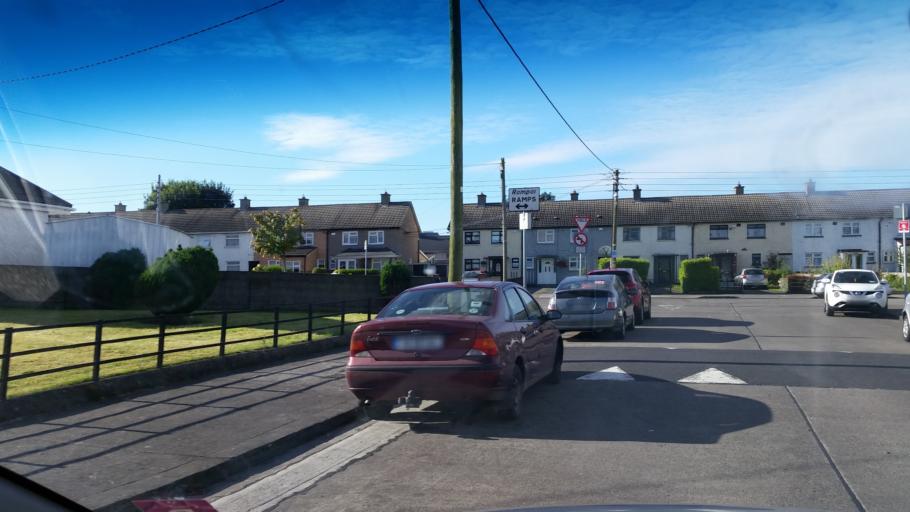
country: IE
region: Leinster
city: Artane
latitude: 53.3937
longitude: -6.2264
